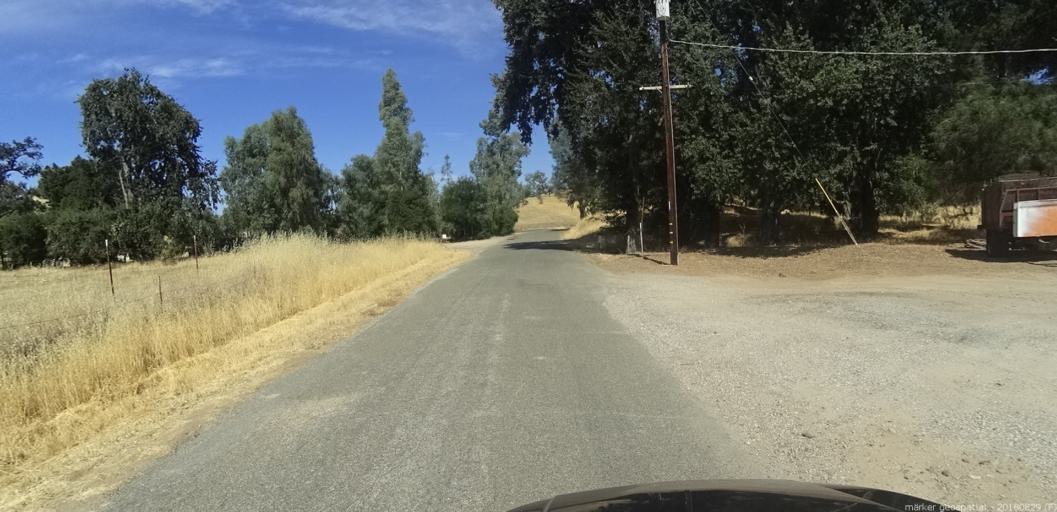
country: US
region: California
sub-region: San Luis Obispo County
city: Lake Nacimiento
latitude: 35.8140
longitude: -121.0914
